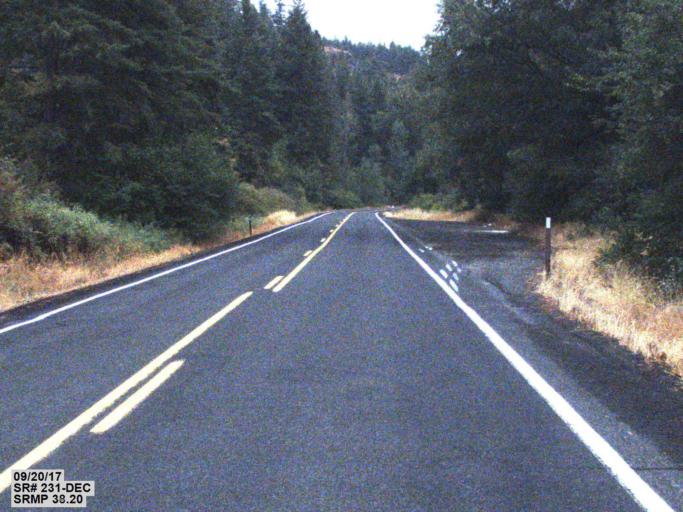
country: US
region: Washington
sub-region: Lincoln County
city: Davenport
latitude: 47.7646
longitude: -117.8913
